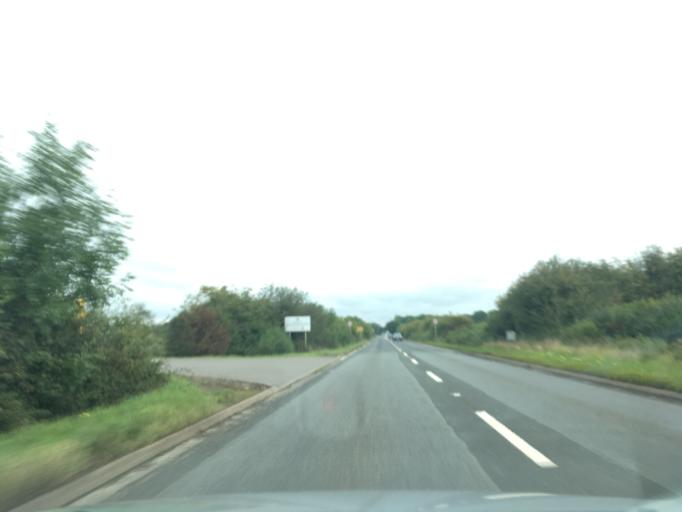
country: GB
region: England
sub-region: Oxfordshire
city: Banbury
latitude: 52.0792
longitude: -1.3134
